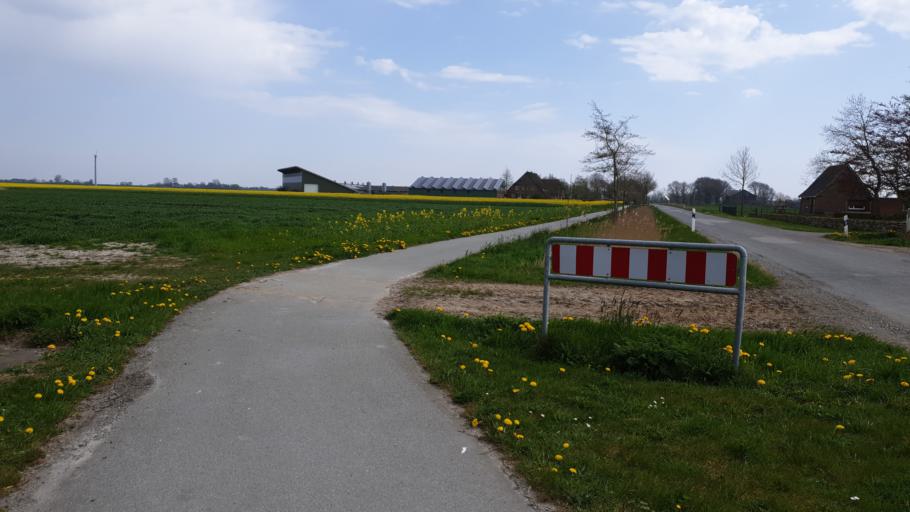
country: DE
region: Schleswig-Holstein
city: Elisabeth-Sophien-Koog
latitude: 54.4757
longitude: 8.8748
